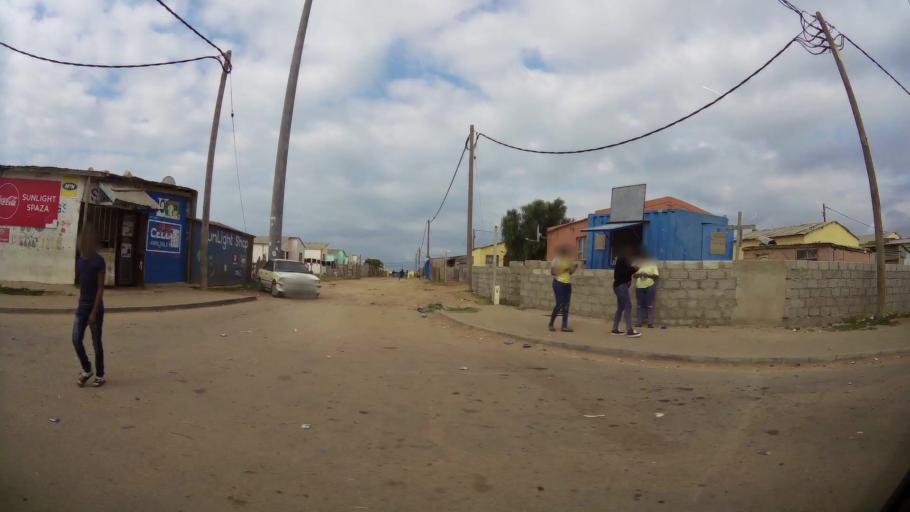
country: ZA
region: Eastern Cape
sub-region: Nelson Mandela Bay Metropolitan Municipality
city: Port Elizabeth
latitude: -33.8283
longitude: 25.6313
